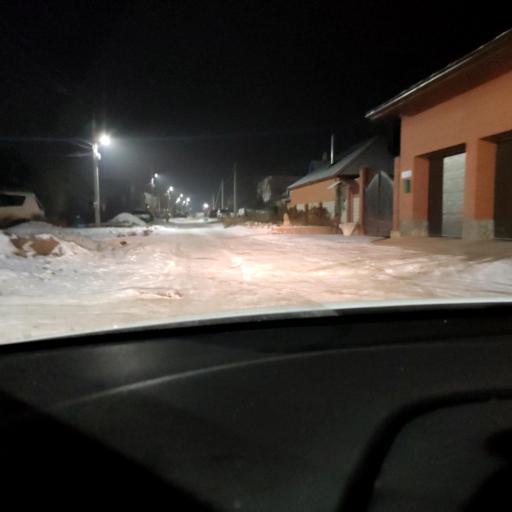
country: RU
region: Tatarstan
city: Staroye Arakchino
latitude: 55.8699
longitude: 49.0383
